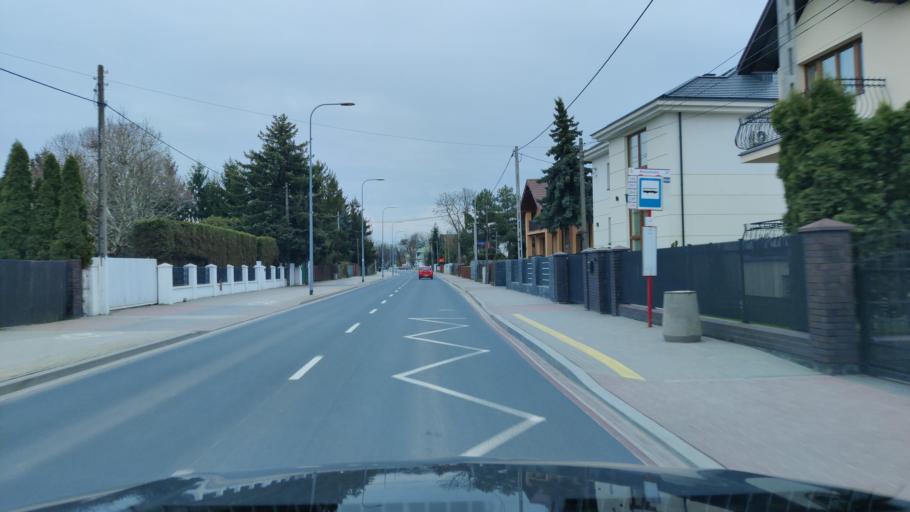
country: PL
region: Masovian Voivodeship
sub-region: Warszawa
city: Kabaty
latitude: 52.1271
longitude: 21.1034
